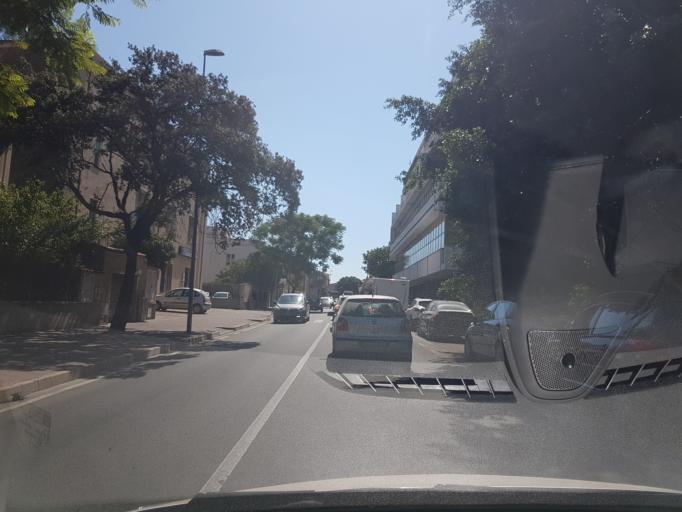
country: IT
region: Sardinia
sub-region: Provincia di Oristano
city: Oristano
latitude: 39.9020
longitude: 8.5894
